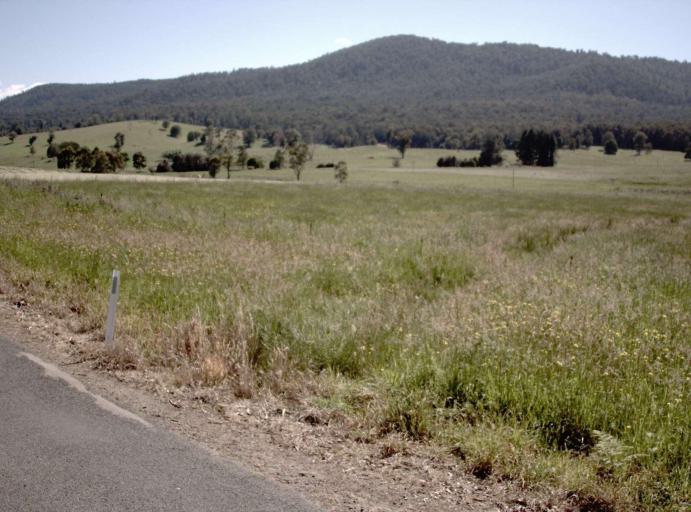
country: AU
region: New South Wales
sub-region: Bombala
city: Bombala
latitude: -37.1874
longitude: 148.7275
